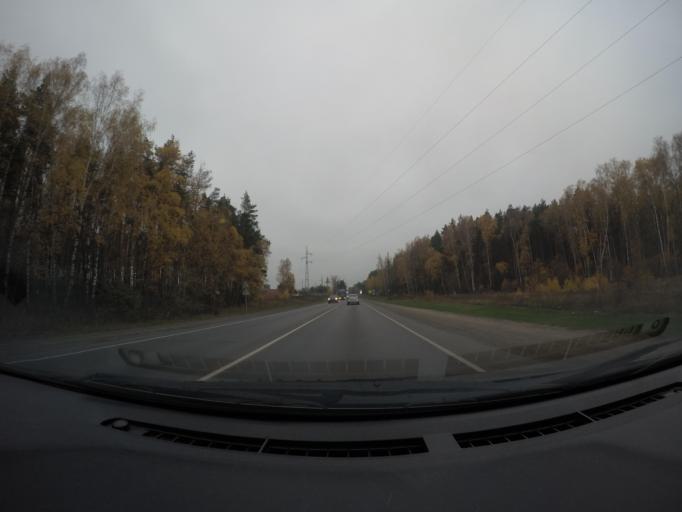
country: RU
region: Moskovskaya
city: Malyshevo
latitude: 55.4762
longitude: 38.3450
